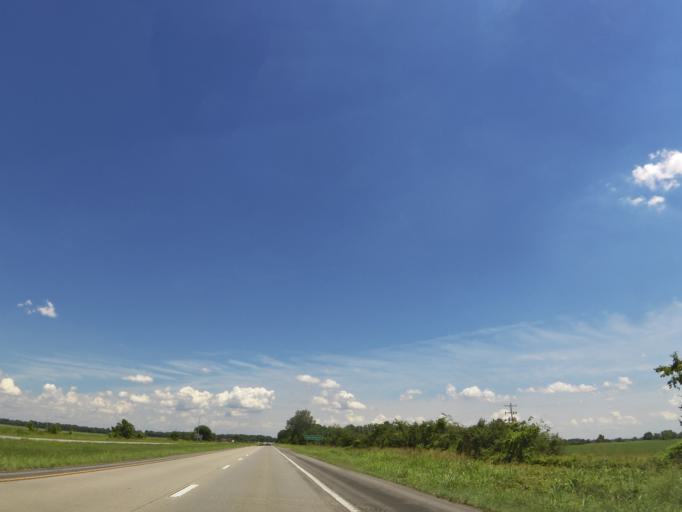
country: US
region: Missouri
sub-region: Pemiscot County
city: Caruthersville
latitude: 36.1459
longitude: -89.6509
